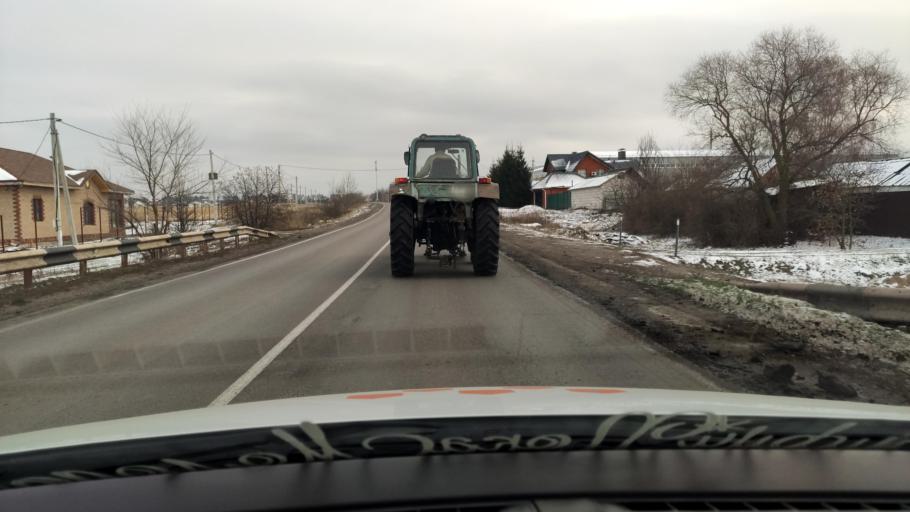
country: RU
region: Voronezj
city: Podgornoye
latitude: 51.8940
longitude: 39.1683
